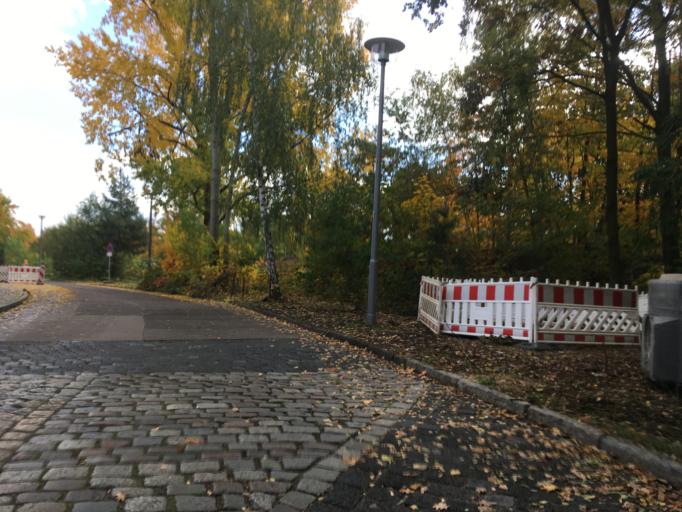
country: DE
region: Berlin
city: Niederschoneweide
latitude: 52.4498
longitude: 13.5242
